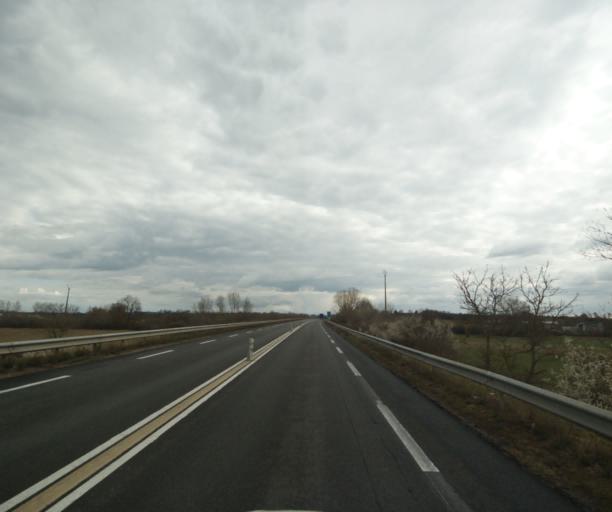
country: FR
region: Auvergne
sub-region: Departement de l'Allier
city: Toulon-sur-Allier
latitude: 46.4924
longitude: 3.3545
